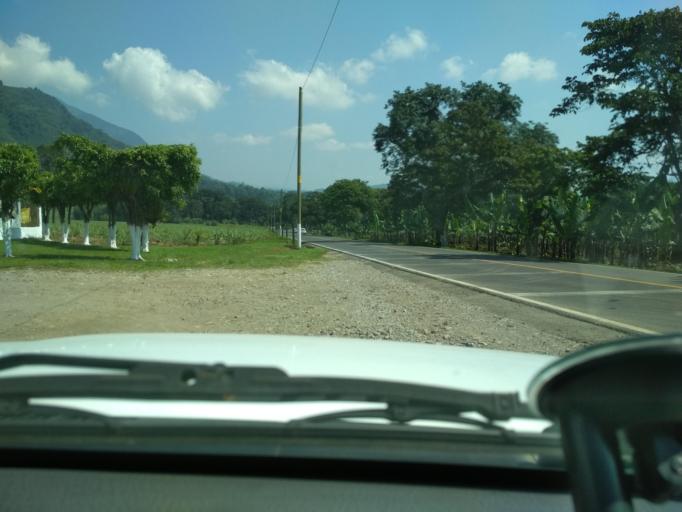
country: MX
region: Veracruz
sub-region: Fortin
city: Santa Lucia Potrerillo
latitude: 18.9799
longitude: -97.0175
